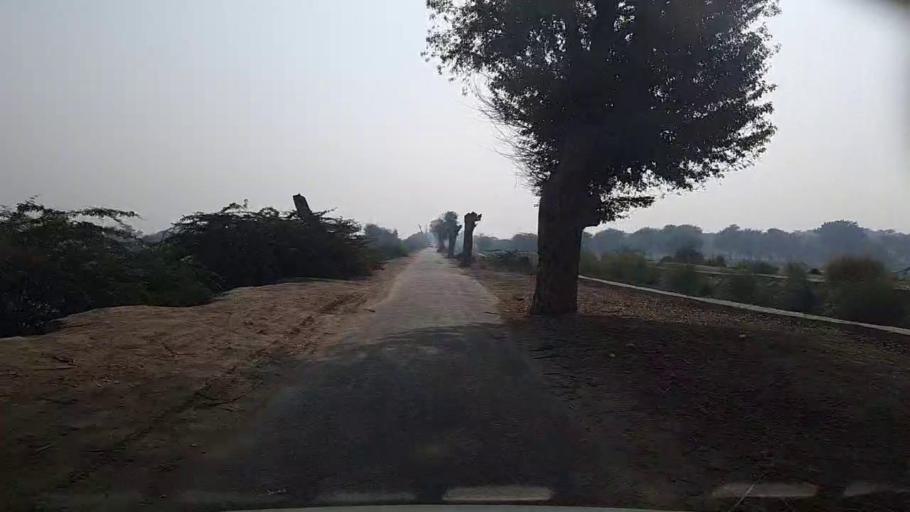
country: PK
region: Sindh
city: Setharja Old
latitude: 27.1052
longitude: 68.5079
